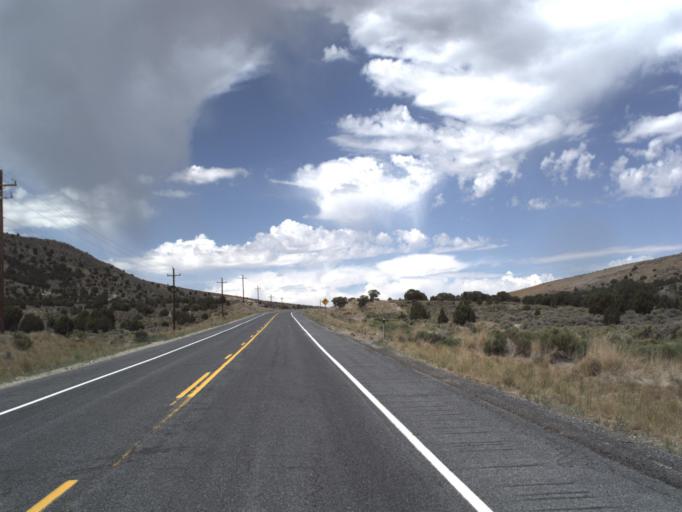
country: US
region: Utah
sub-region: Utah County
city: Eagle Mountain
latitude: 40.0742
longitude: -112.3575
